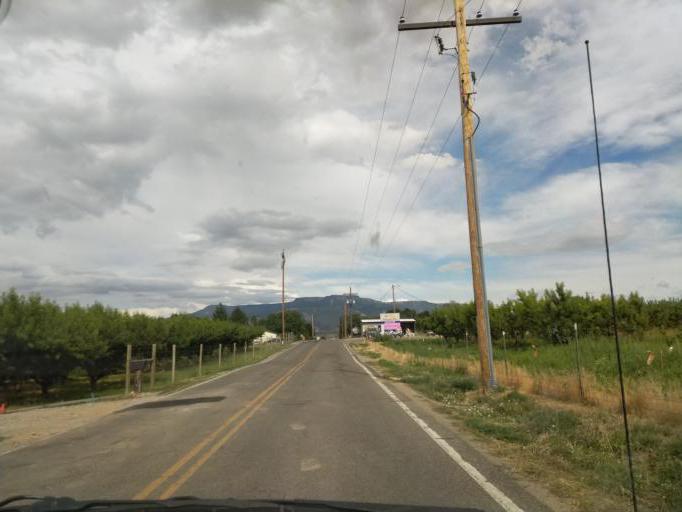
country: US
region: Colorado
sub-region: Mesa County
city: Clifton
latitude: 39.0558
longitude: -108.4193
